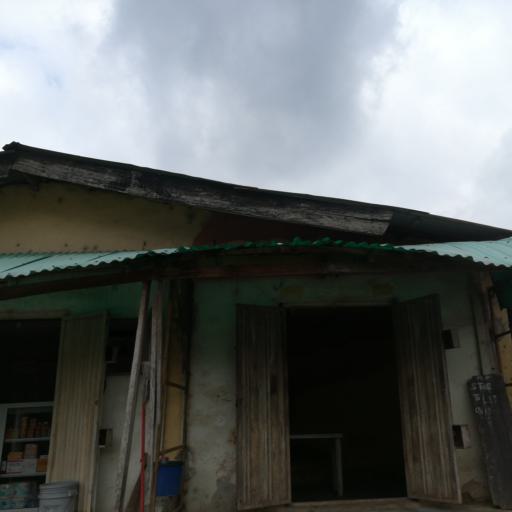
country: NG
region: Rivers
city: Port Harcourt
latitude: 4.8318
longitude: 7.0708
